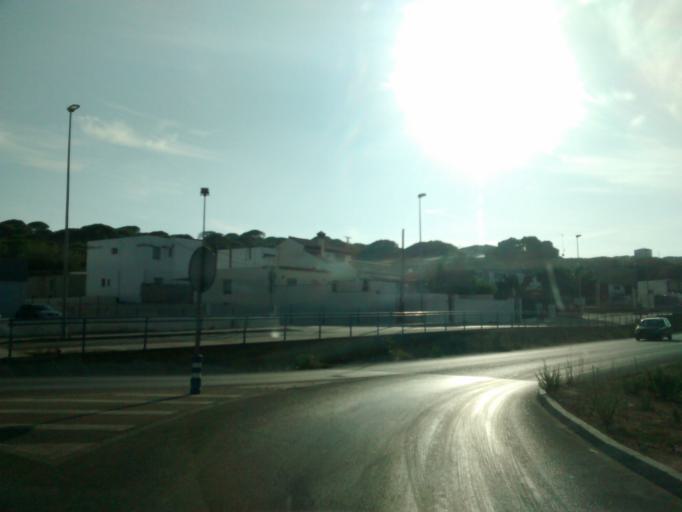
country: ES
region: Andalusia
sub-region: Provincia de Cadiz
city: Barbate de Franco
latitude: 36.2021
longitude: -5.9253
